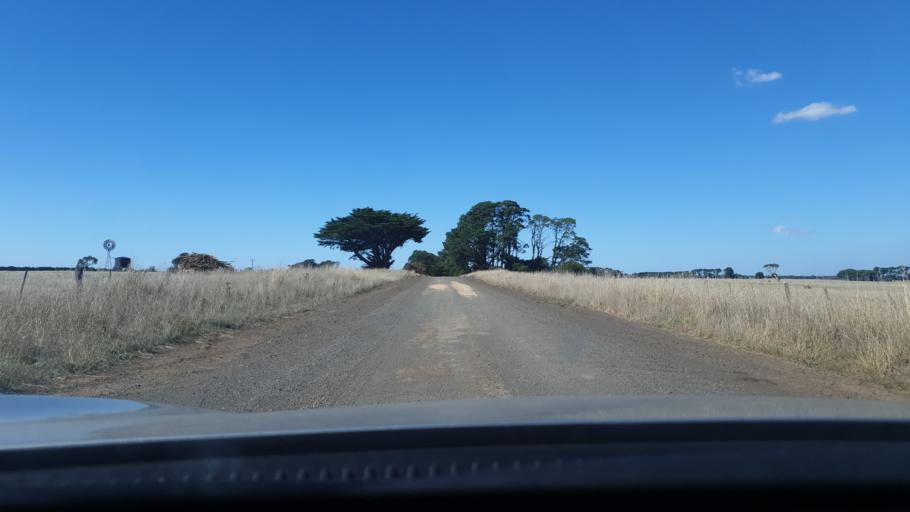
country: AU
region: Victoria
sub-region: Warrnambool
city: Warrnambool
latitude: -38.1648
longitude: 142.3852
